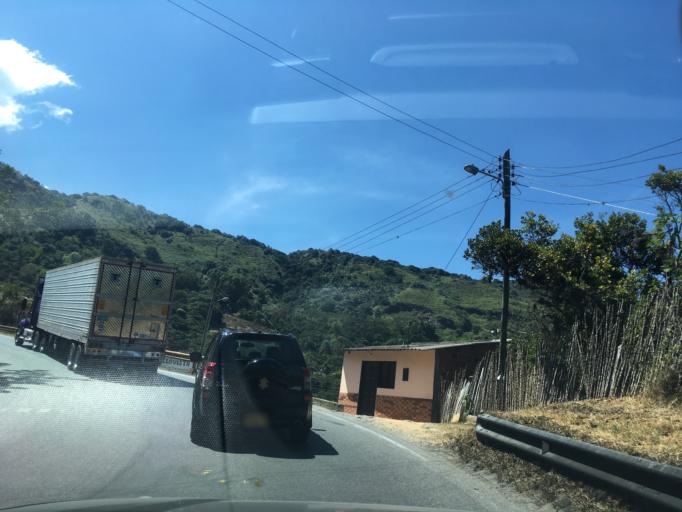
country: CO
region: Santander
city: Aratoca
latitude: 6.6923
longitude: -73.0172
